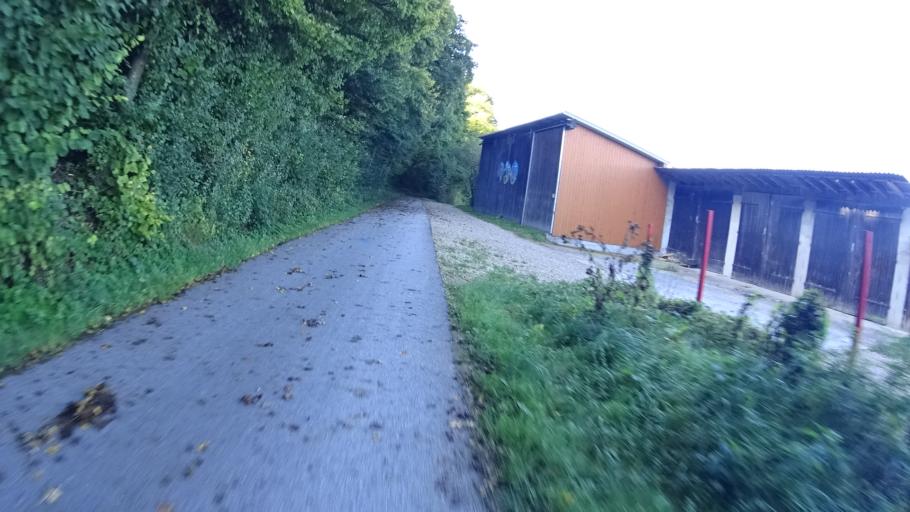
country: DE
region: Bavaria
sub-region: Upper Bavaria
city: Eichstaett
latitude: 48.8748
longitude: 11.2340
